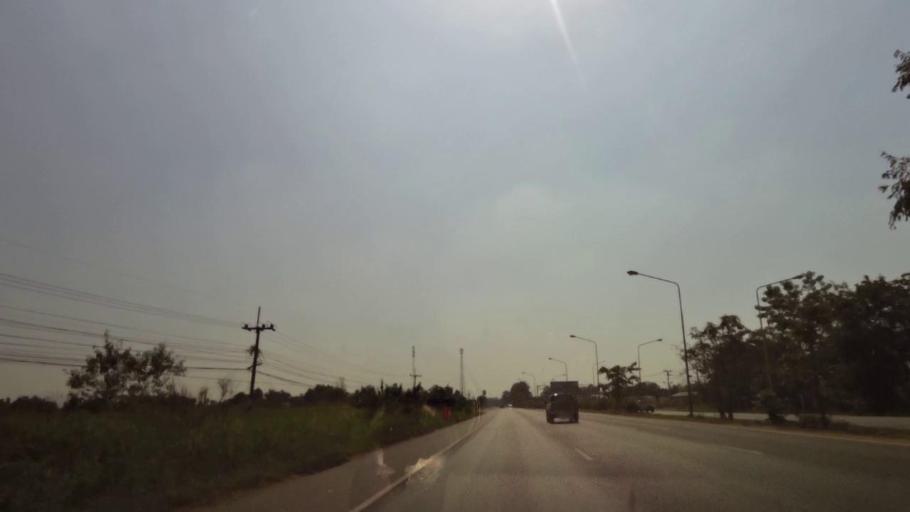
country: TH
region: Phichit
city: Wachira Barami
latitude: 16.3501
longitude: 100.1286
